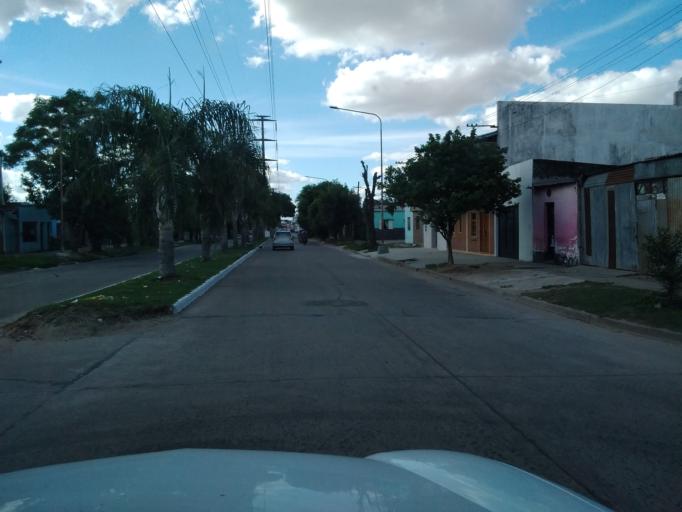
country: AR
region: Corrientes
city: Corrientes
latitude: -27.4879
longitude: -58.8380
